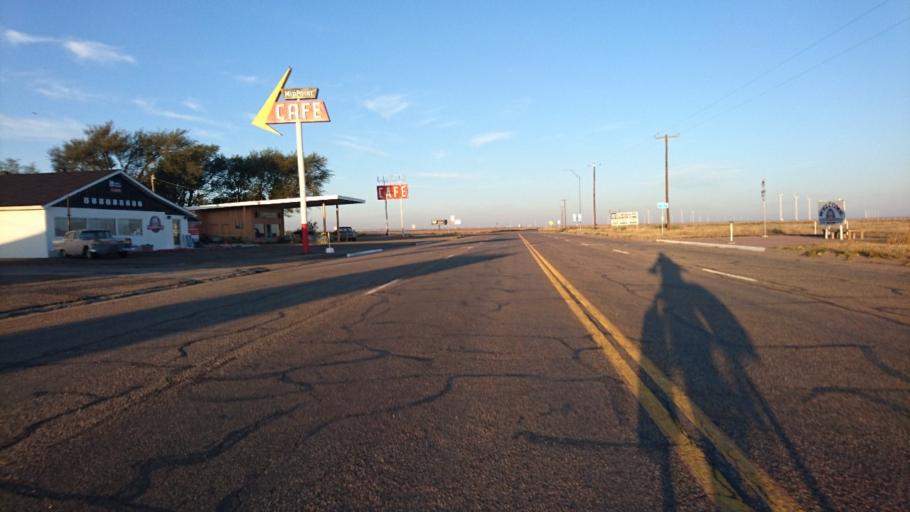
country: US
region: Texas
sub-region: Oldham County
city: Vega
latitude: 35.2710
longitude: -102.6724
